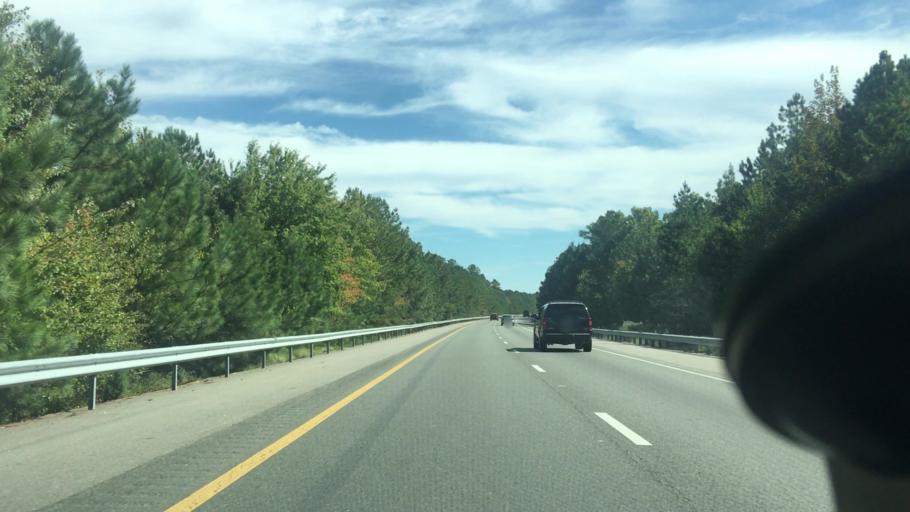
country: US
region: Virginia
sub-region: Chesterfield County
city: Chesterfield
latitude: 37.4067
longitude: -77.5467
